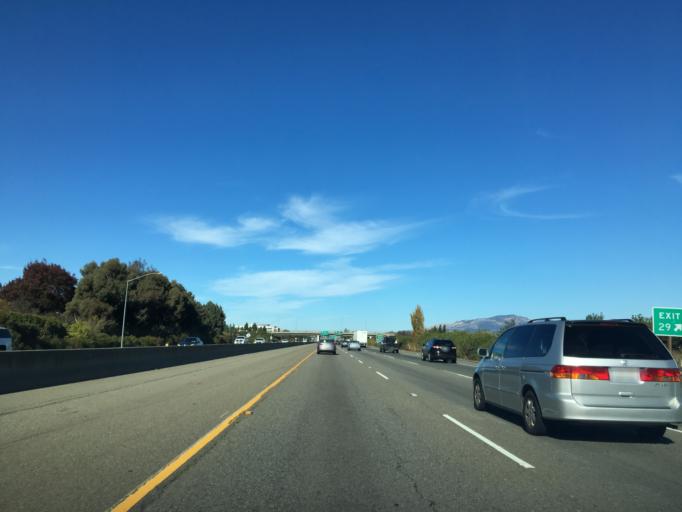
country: US
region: California
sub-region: Alameda County
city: Dublin
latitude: 37.6866
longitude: -121.9170
